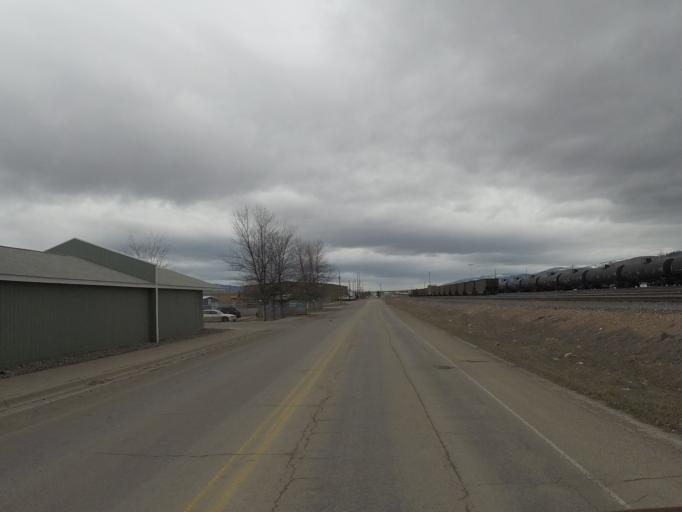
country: US
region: Montana
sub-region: Missoula County
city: Missoula
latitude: 46.8902
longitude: -114.0222
